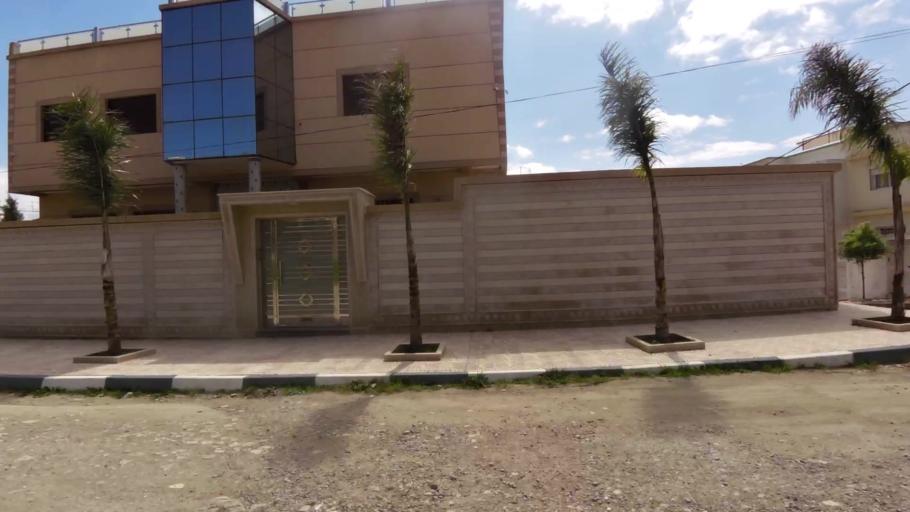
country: MA
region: Tanger-Tetouan
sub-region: Tanger-Assilah
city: Tangier
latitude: 35.7659
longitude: -5.8412
